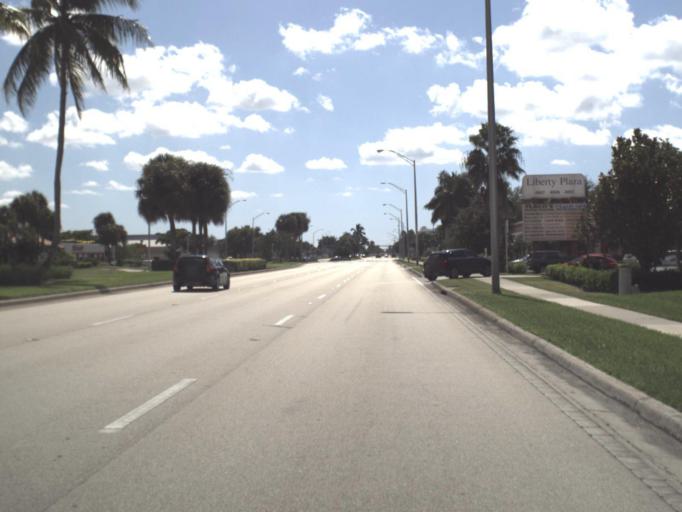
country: US
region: Florida
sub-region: Collier County
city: Pine Ridge
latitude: 26.2080
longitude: -81.8005
